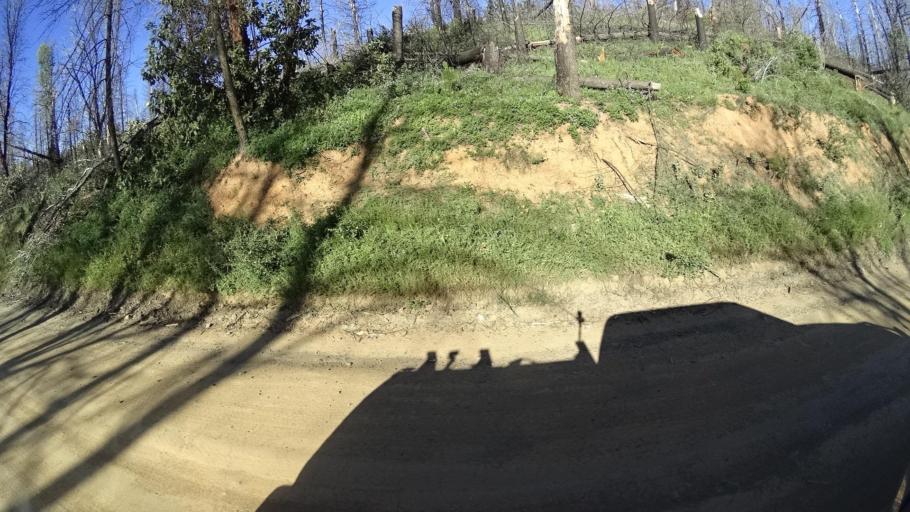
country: US
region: California
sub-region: Lake County
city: Upper Lake
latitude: 39.3388
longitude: -122.9579
